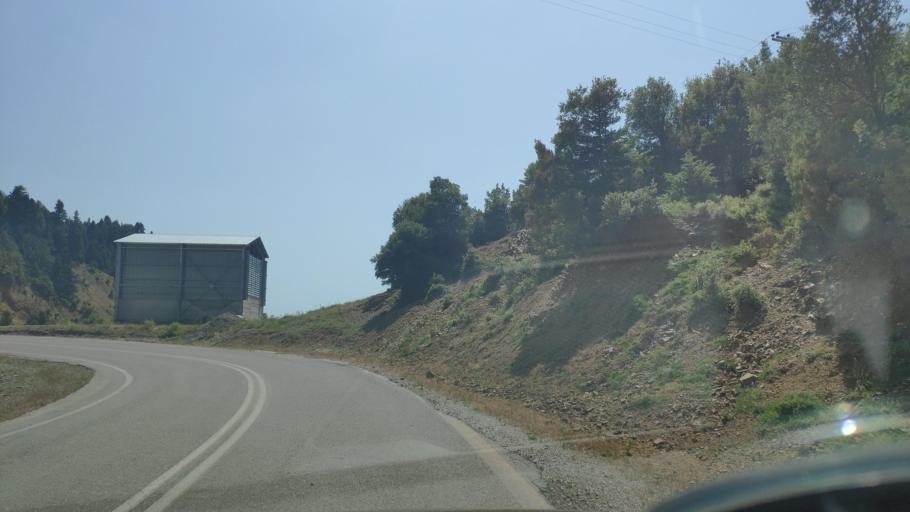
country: GR
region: Epirus
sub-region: Nomos Artas
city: Ano Kalentini
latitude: 39.2407
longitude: 21.2310
